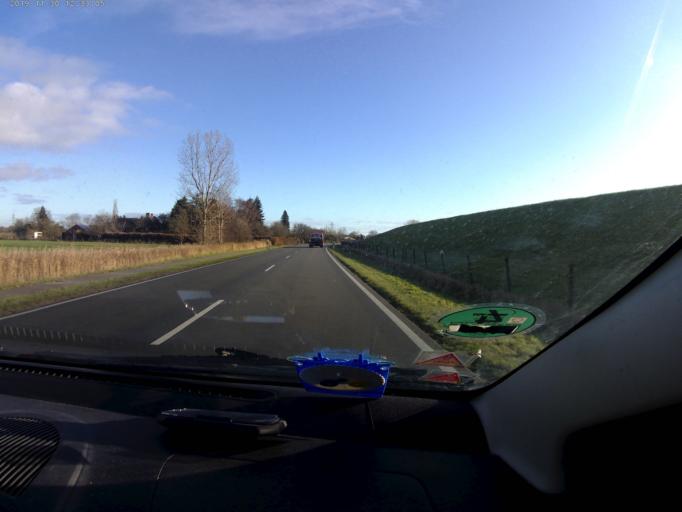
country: DE
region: Lower Saxony
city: Leer
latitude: 53.2332
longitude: 7.4205
